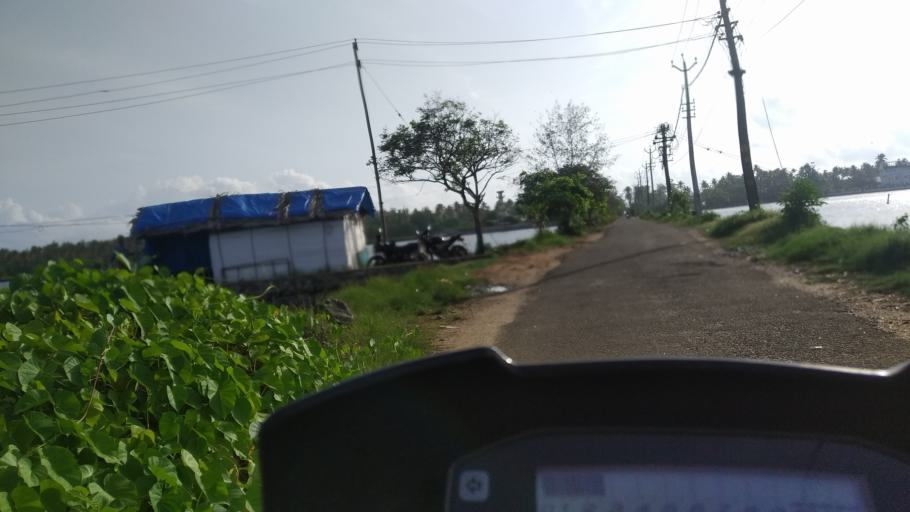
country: IN
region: Kerala
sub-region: Thrissur District
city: Kodungallur
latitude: 10.1282
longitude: 76.1873
